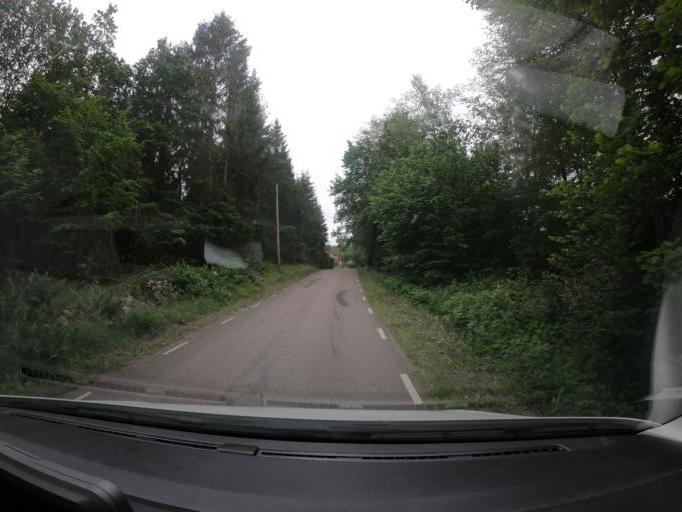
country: SE
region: Skane
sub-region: Perstorps Kommun
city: Perstorp
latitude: 56.0937
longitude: 13.3302
